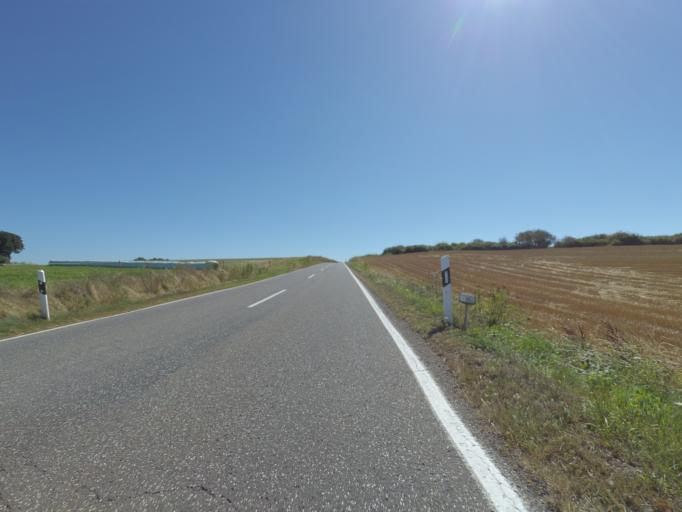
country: DE
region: Rheinland-Pfalz
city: Urschmitt
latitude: 50.1055
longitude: 7.0652
